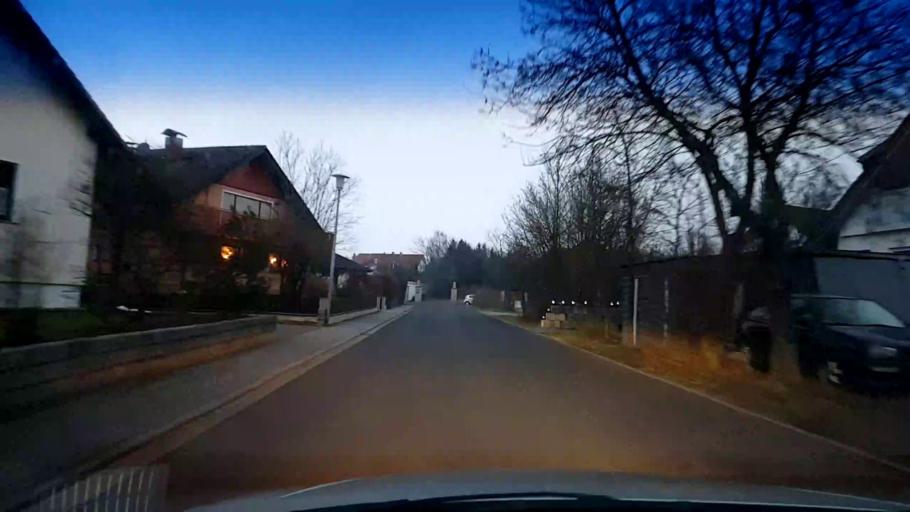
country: DE
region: Bavaria
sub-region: Upper Franconia
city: Rattelsdorf
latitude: 50.0149
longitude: 10.8963
